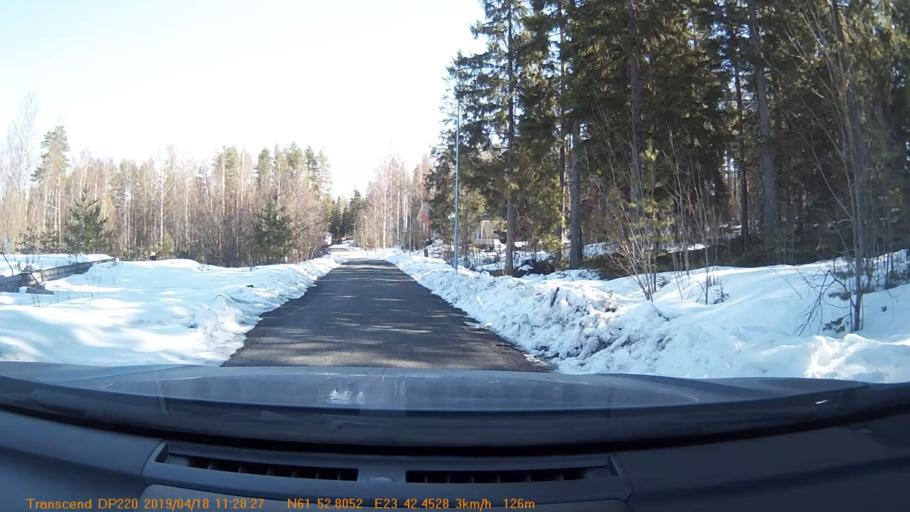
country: FI
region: Pirkanmaa
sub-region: Tampere
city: Kuru
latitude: 61.8800
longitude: 23.7074
